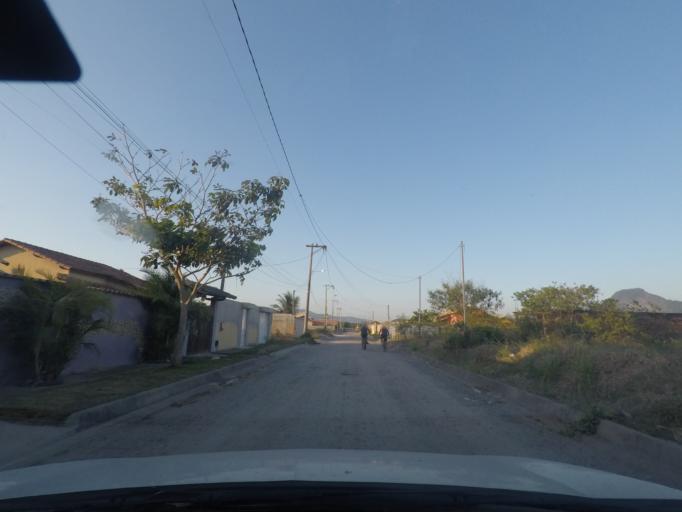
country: BR
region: Rio de Janeiro
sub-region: Marica
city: Marica
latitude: -22.9613
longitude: -42.9415
